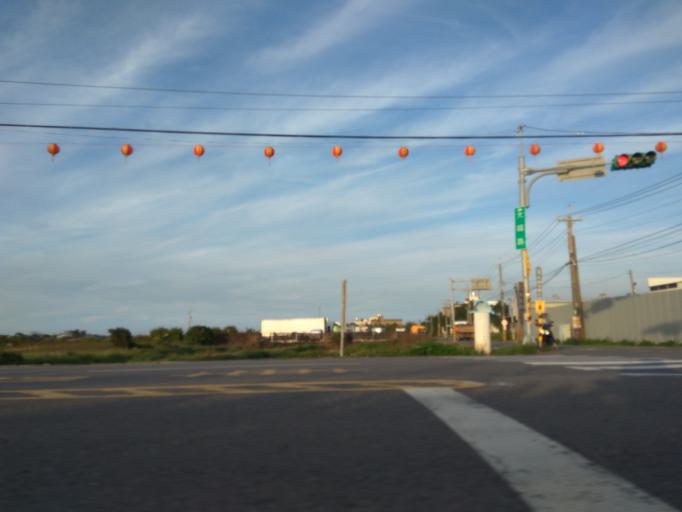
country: TW
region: Taiwan
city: Taoyuan City
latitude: 25.0068
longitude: 121.1458
